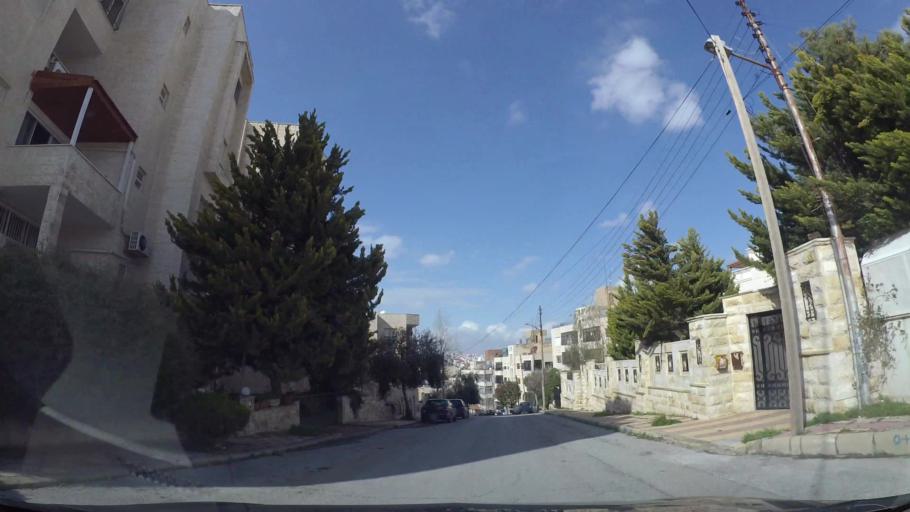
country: JO
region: Amman
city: Al Jubayhah
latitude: 31.9740
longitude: 35.8903
